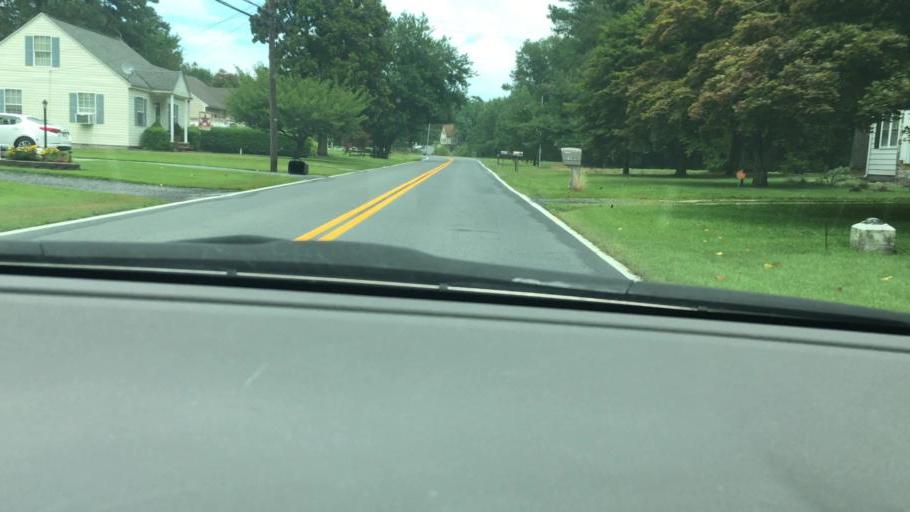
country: US
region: Maryland
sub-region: Worcester County
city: Pocomoke City
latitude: 38.0621
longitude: -75.5428
